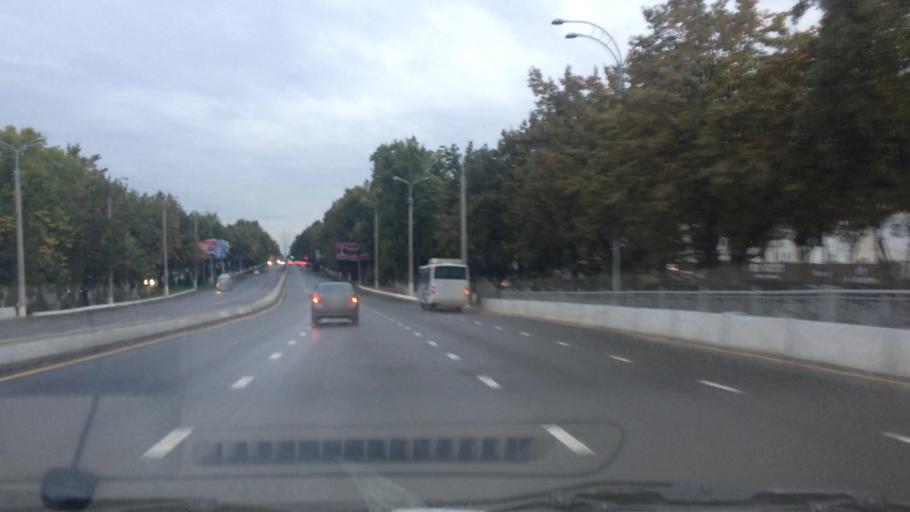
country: UZ
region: Toshkent Shahri
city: Tashkent
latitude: 41.2733
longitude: 69.2037
